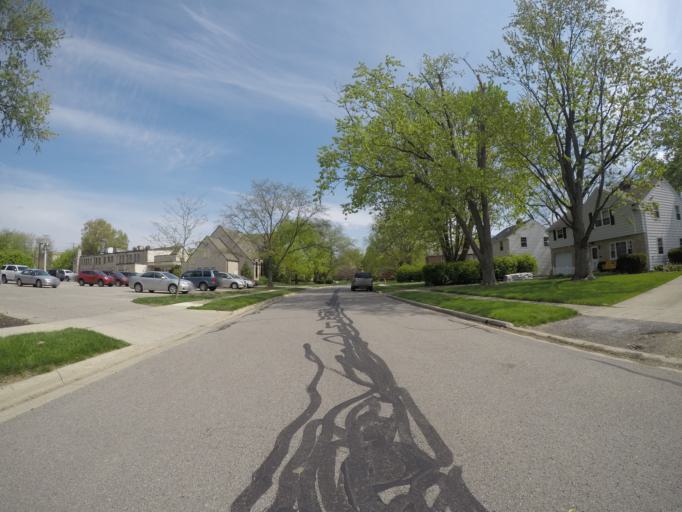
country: US
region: Ohio
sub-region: Franklin County
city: Upper Arlington
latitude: 39.9970
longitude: -83.0519
